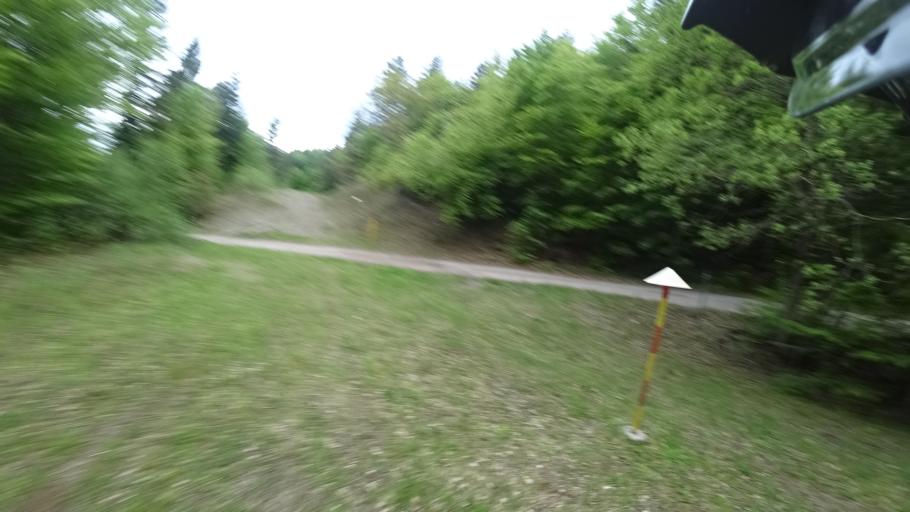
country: HR
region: Licko-Senjska
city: Jezerce
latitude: 44.8808
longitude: 15.4321
